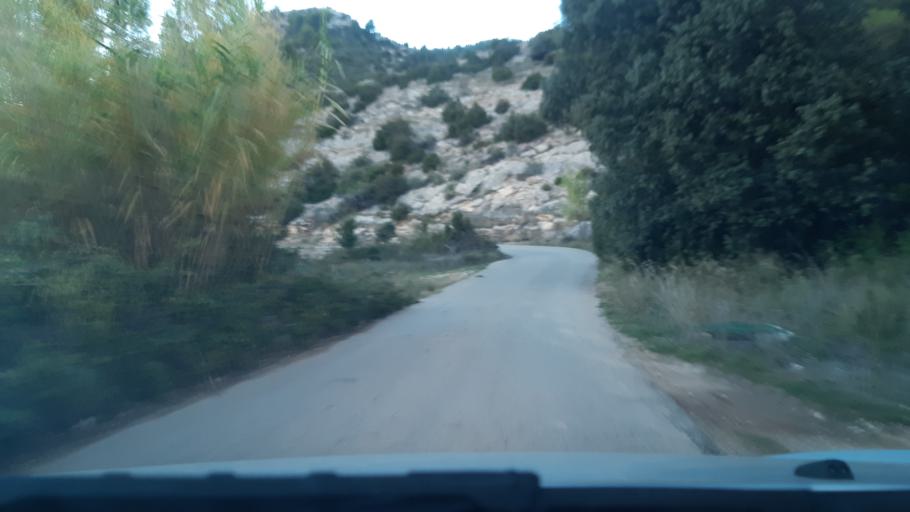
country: ES
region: Aragon
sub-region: Provincia de Teruel
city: Valderrobres
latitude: 40.8395
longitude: 0.1873
